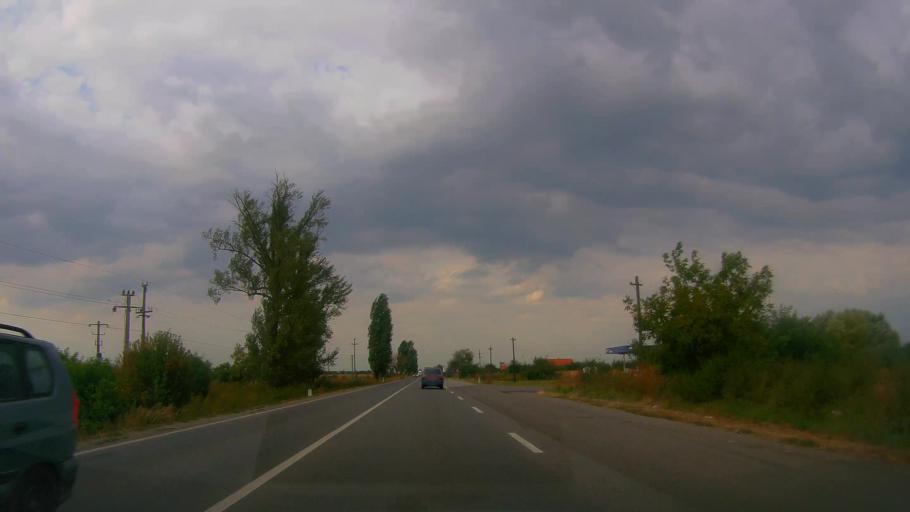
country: RO
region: Satu Mare
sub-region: Comuna Botiz
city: Botiz
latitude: 47.8169
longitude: 22.9316
